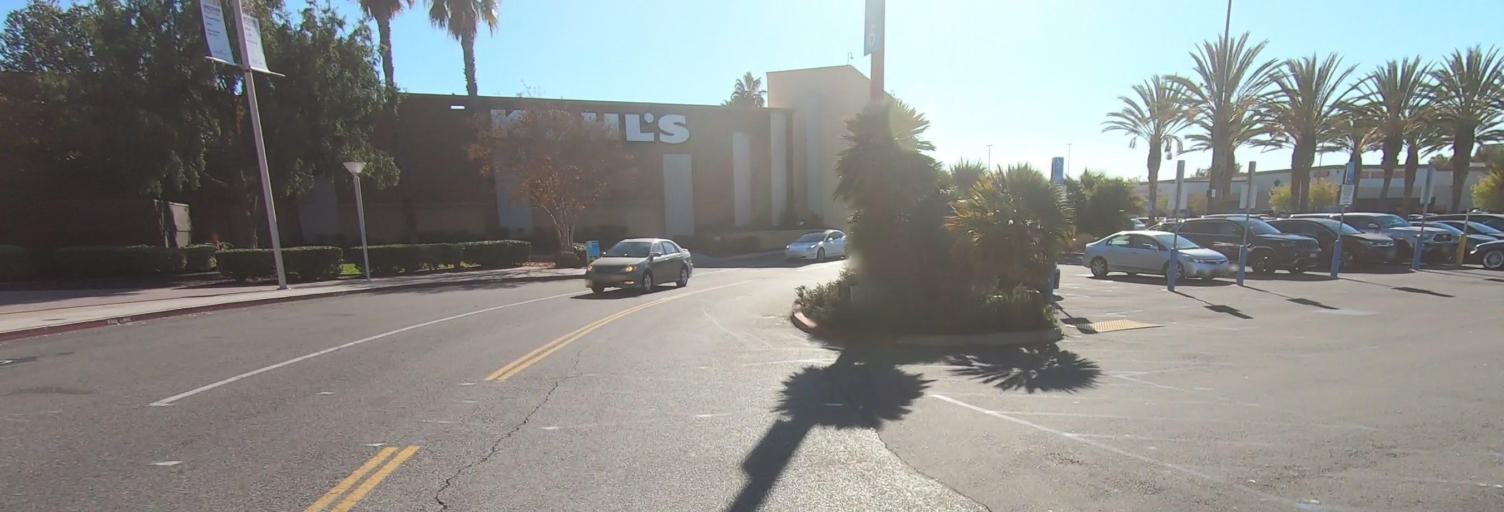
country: US
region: California
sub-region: Santa Clara County
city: Milpitas
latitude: 37.4176
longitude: -121.8997
